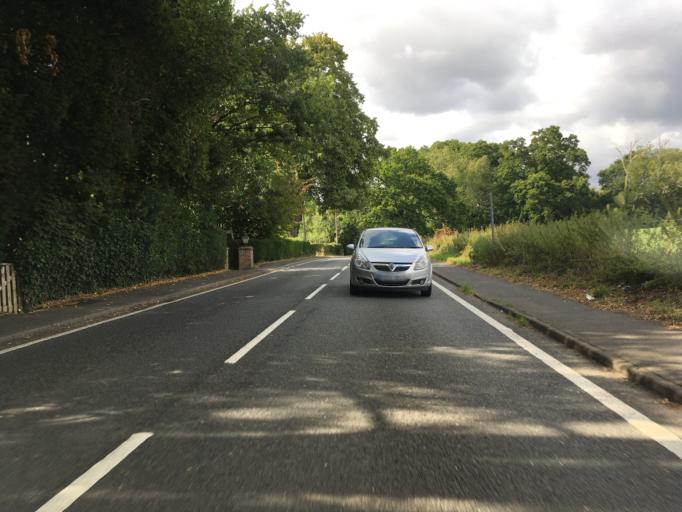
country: GB
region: England
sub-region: Hampshire
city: Colden Common
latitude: 51.0010
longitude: -1.3171
